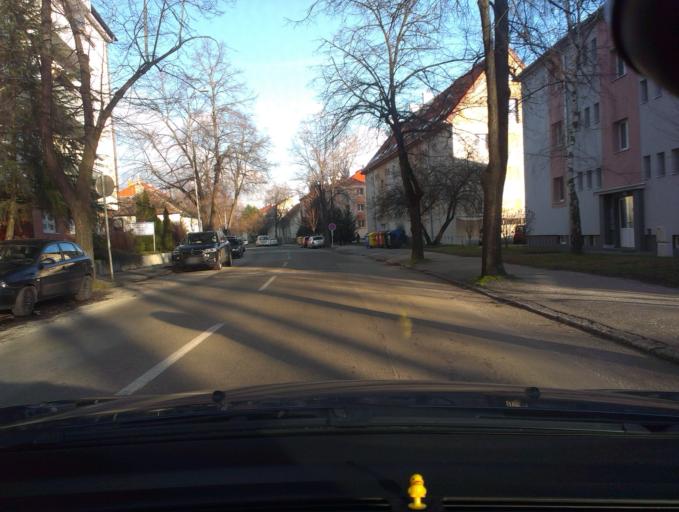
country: SK
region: Trnavsky
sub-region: Okres Trnava
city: Piestany
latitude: 48.5956
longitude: 17.8342
